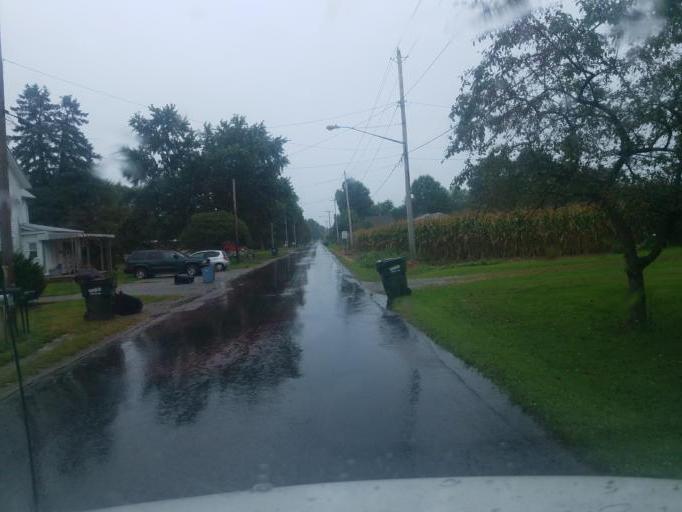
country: US
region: Ohio
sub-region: Wayne County
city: Creston
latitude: 40.9861
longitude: -81.8898
